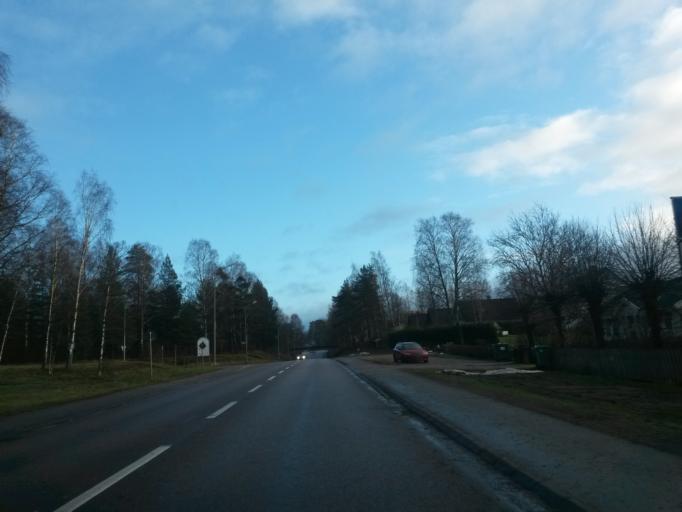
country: SE
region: Vaestra Goetaland
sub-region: Boras Kommun
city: Boras
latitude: 57.8260
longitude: 13.0042
